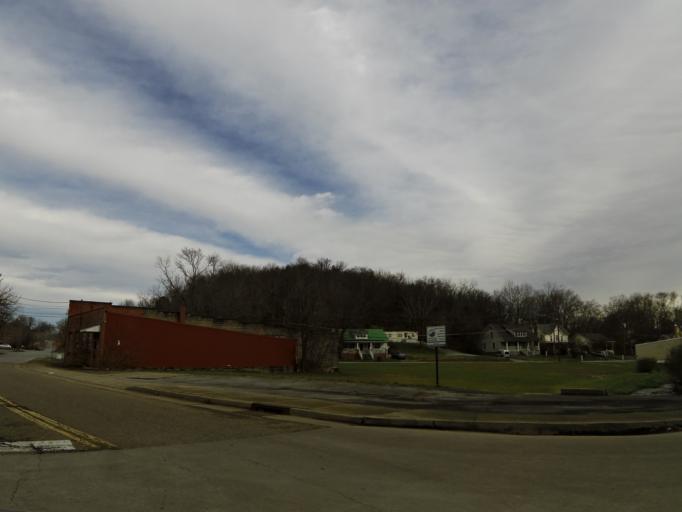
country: US
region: Tennessee
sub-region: Greene County
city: Greeneville
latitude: 36.1600
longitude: -82.8309
